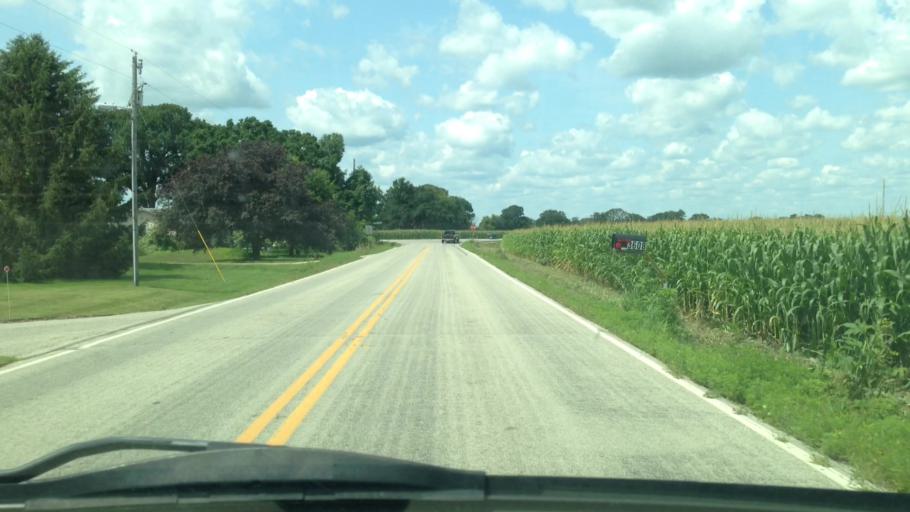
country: US
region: Minnesota
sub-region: Olmsted County
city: Rochester
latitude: 43.9531
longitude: -92.5166
